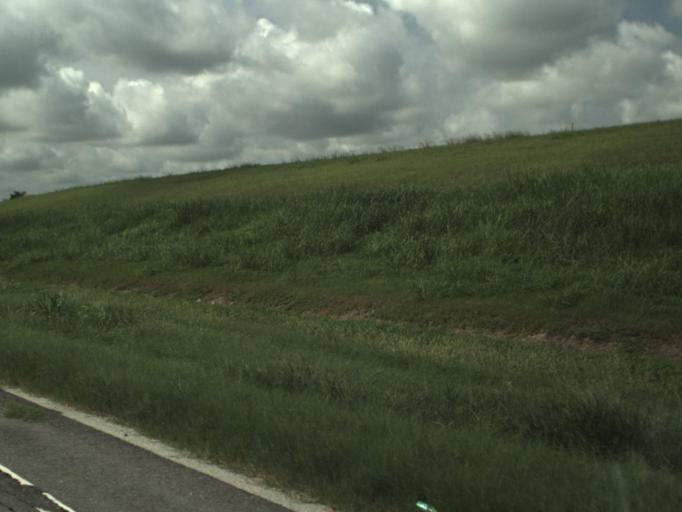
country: US
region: Florida
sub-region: Palm Beach County
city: Pahokee
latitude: 26.7532
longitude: -80.6833
